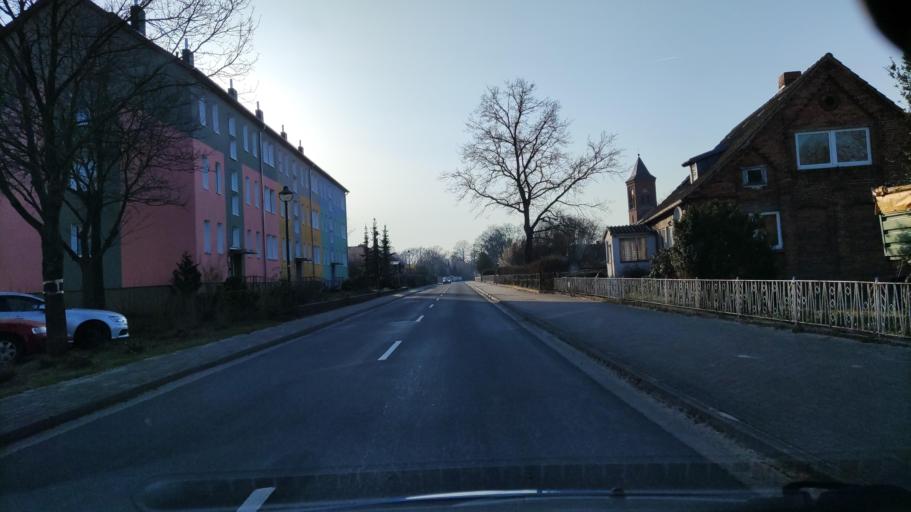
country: DE
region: Brandenburg
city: Lanz
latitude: 52.9928
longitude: 11.5803
